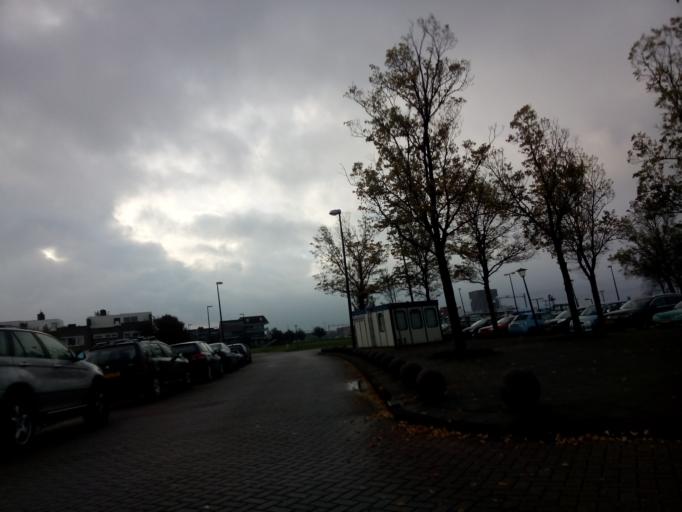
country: NL
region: South Holland
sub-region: Gemeente Maassluis
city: Maassluis
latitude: 51.9269
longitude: 4.2358
